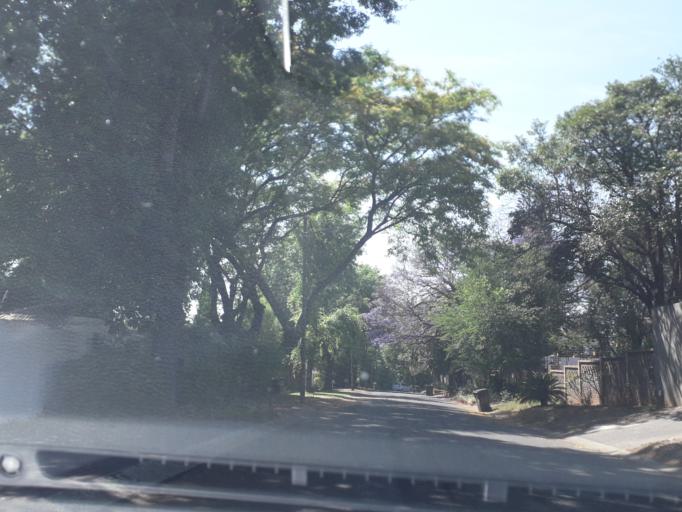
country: ZA
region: Gauteng
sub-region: City of Johannesburg Metropolitan Municipality
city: Johannesburg
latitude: -26.1109
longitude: 28.0035
